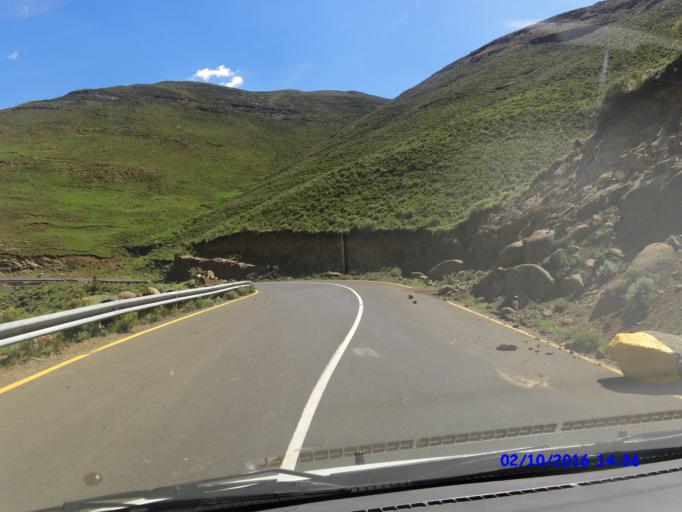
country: LS
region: Maseru
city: Nako
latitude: -29.4993
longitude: 28.0616
